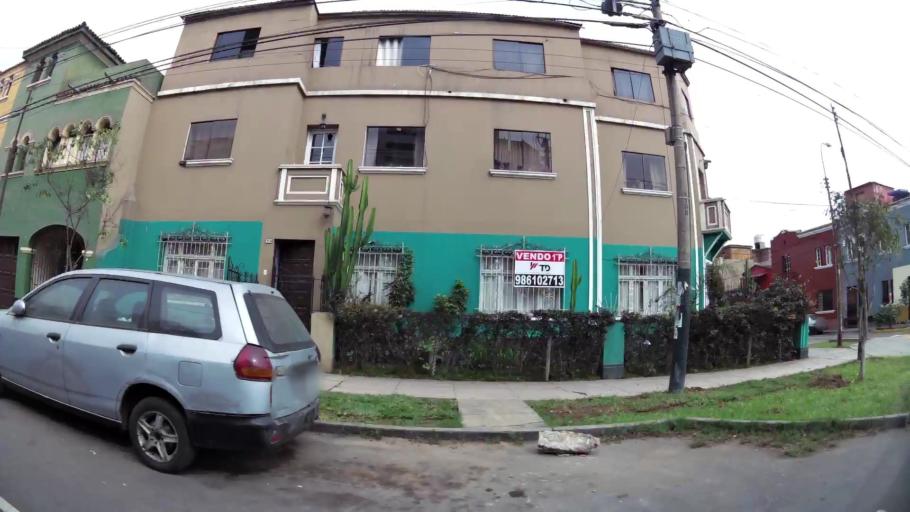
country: PE
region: Lima
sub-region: Lima
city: San Isidro
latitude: -12.0838
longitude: -77.0447
